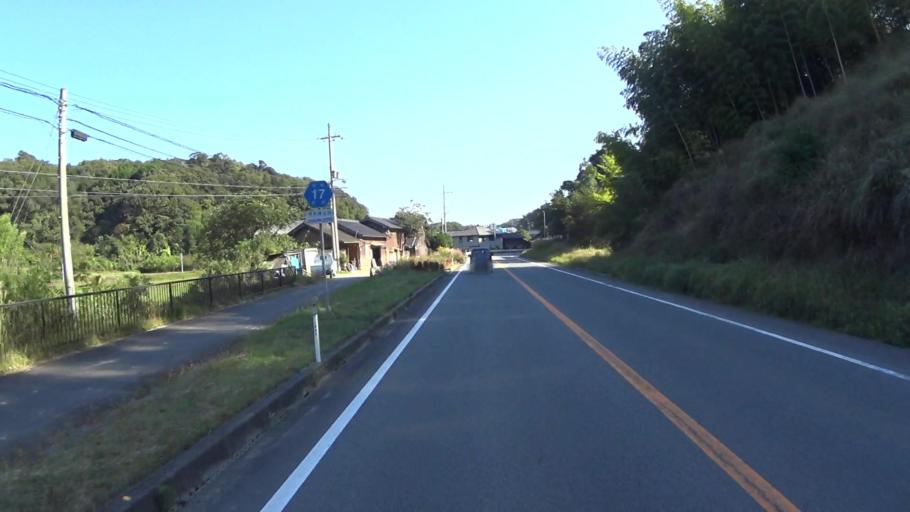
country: JP
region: Kyoto
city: Miyazu
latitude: 35.6422
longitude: 135.0517
